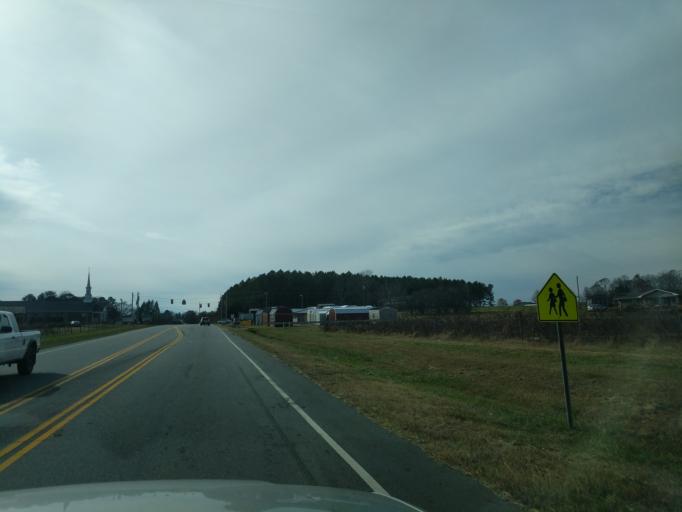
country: US
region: South Carolina
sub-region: Oconee County
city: Walhalla
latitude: 34.7823
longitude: -83.0187
